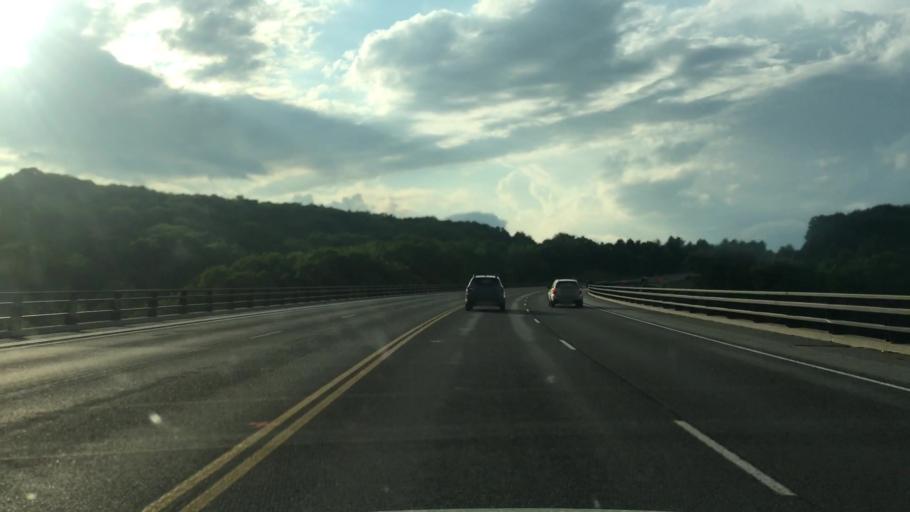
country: US
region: Maine
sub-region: Kennebec County
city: Augusta
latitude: 44.3347
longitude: -69.7638
